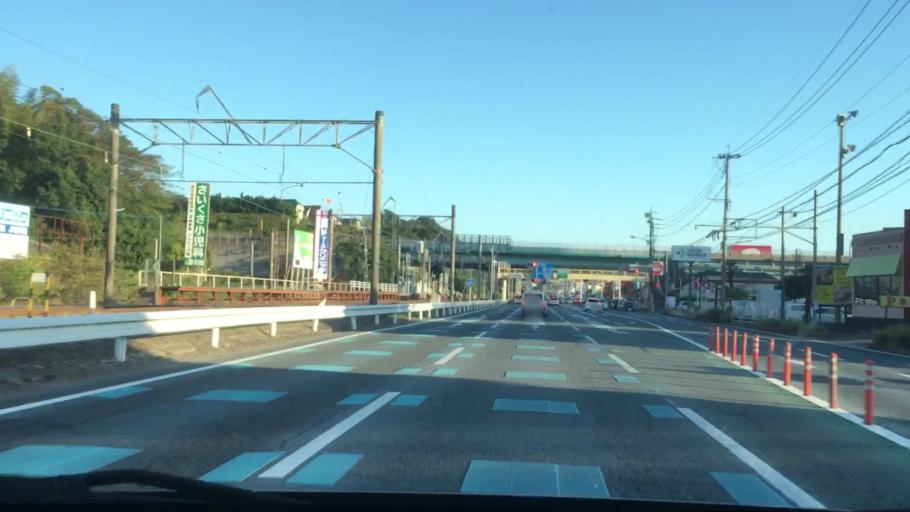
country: JP
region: Nagasaki
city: Sasebo
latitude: 33.1502
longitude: 129.7809
